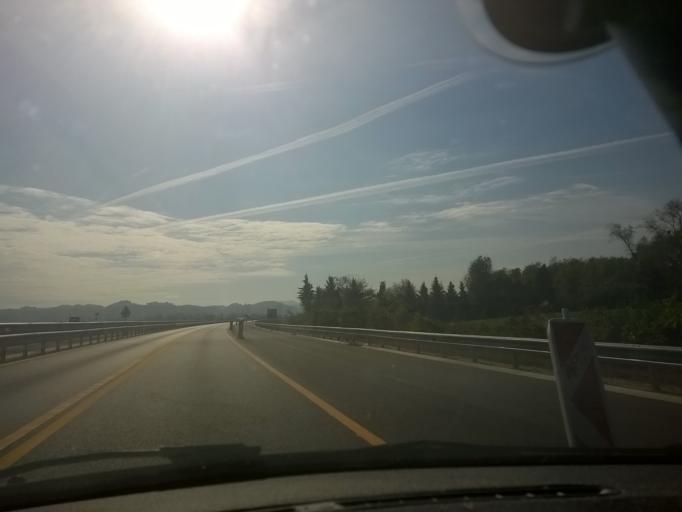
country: SI
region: Hajdina
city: Spodnja Hajdina
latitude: 46.3855
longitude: 15.8644
